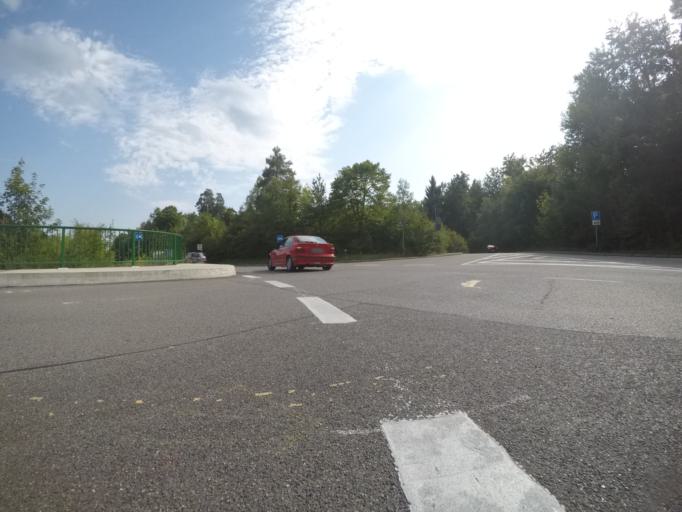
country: DE
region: Baden-Wuerttemberg
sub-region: Regierungsbezirk Stuttgart
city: Gerlingen
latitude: 48.7782
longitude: 9.0899
